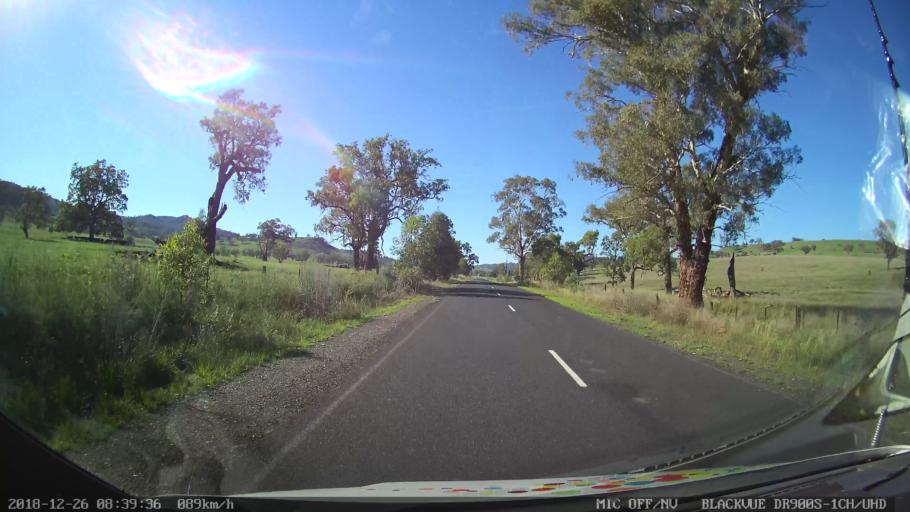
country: AU
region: New South Wales
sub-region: Mid-Western Regional
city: Kandos
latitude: -32.4557
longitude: 150.0756
